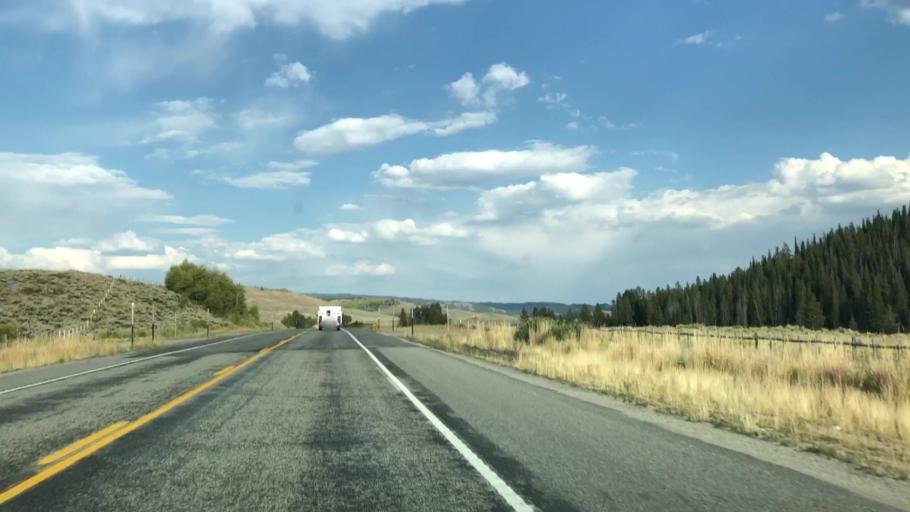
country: US
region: Wyoming
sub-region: Teton County
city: Hoback
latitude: 43.1559
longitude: -110.3154
